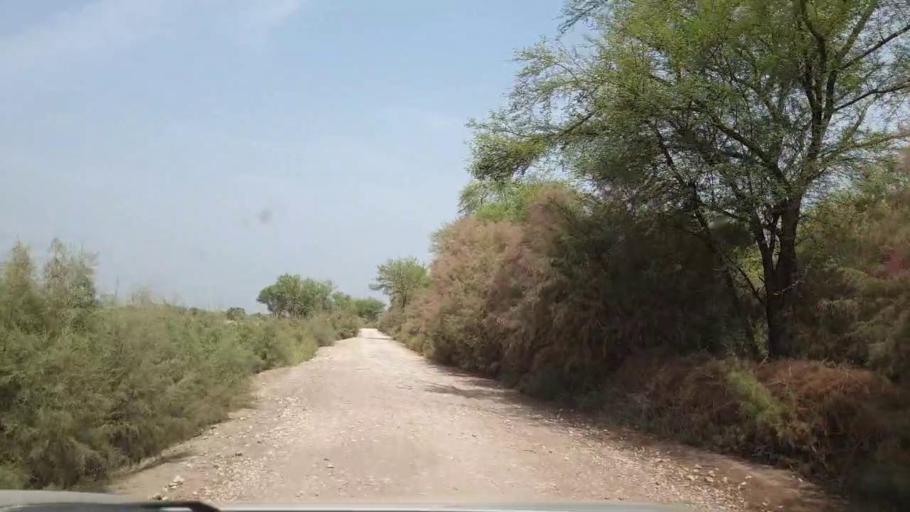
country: PK
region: Sindh
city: Sobhadero
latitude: 27.3955
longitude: 68.2607
